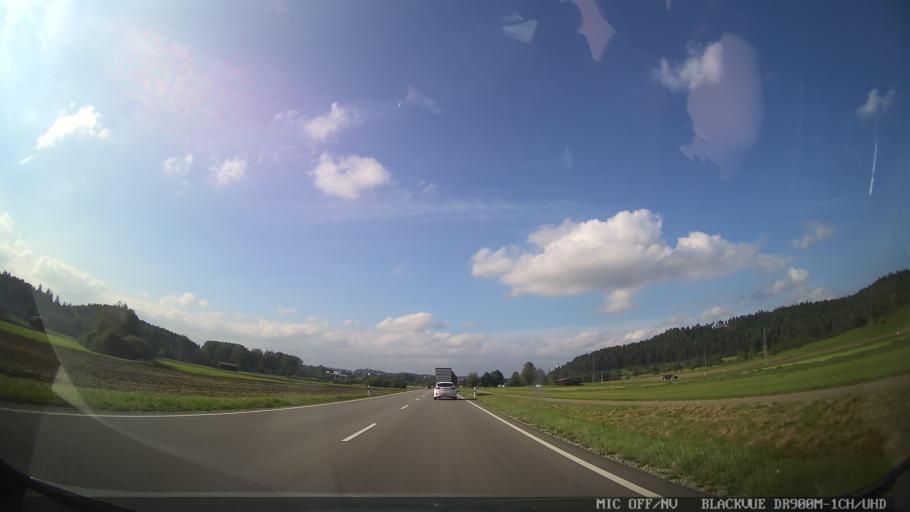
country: DE
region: Baden-Wuerttemberg
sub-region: Freiburg Region
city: Rottweil
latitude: 48.1357
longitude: 8.6588
